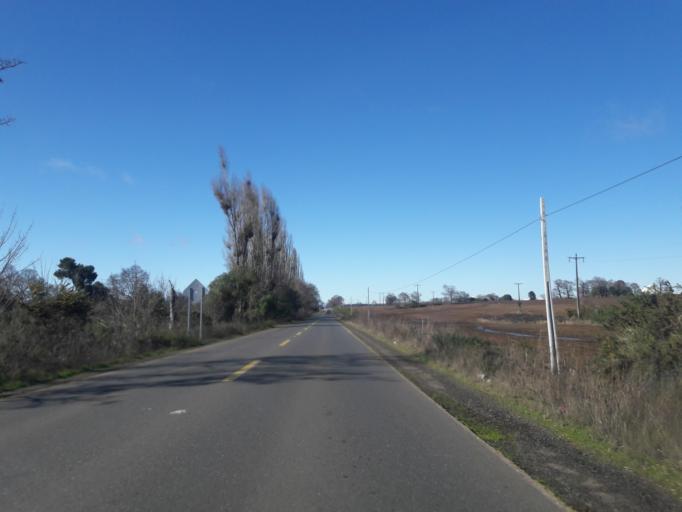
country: CL
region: Araucania
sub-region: Provincia de Malleco
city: Victoria
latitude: -38.2583
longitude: -72.2613
